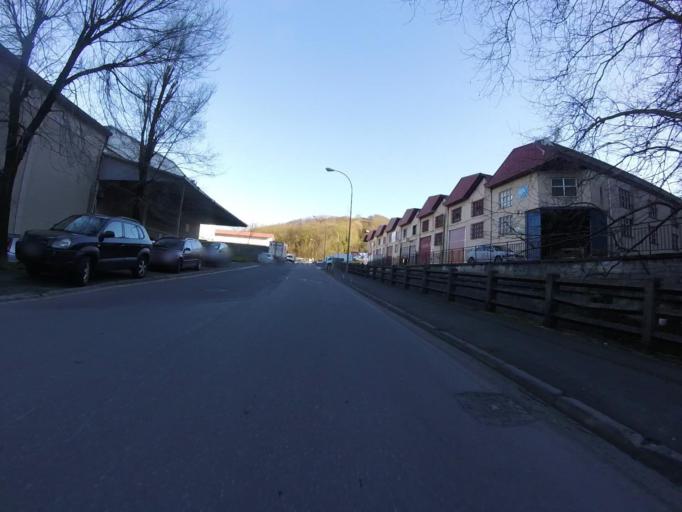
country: ES
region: Basque Country
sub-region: Provincia de Guipuzcoa
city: Errenteria
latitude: 43.2932
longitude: -1.8845
